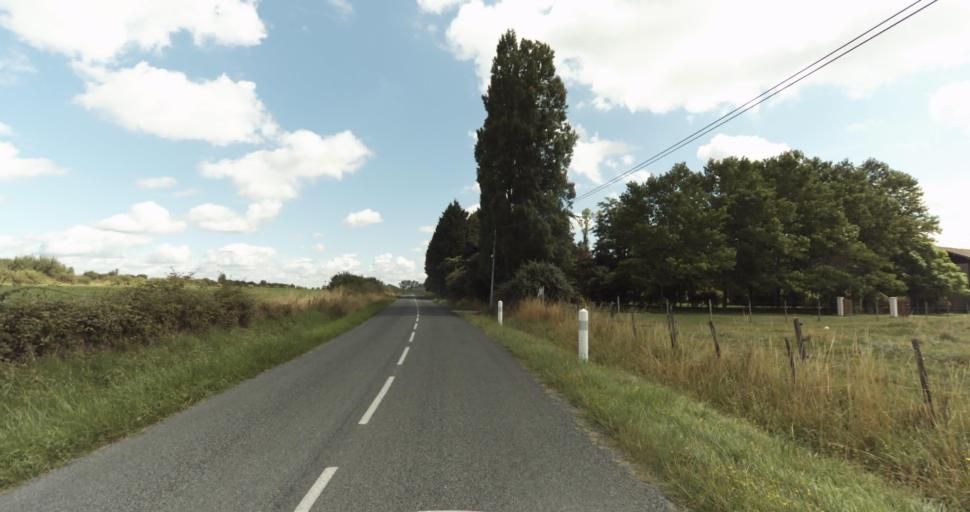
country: FR
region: Aquitaine
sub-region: Departement de la Gironde
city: Bazas
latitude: 44.4604
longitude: -0.1885
